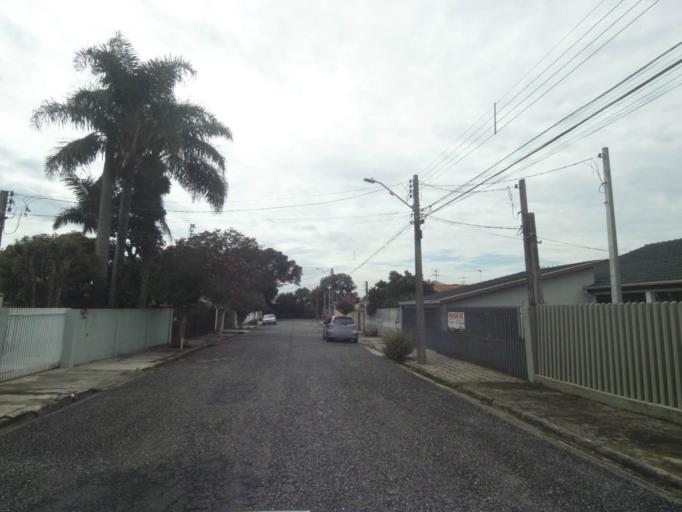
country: BR
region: Parana
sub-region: Pinhais
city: Pinhais
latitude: -25.4722
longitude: -49.1995
